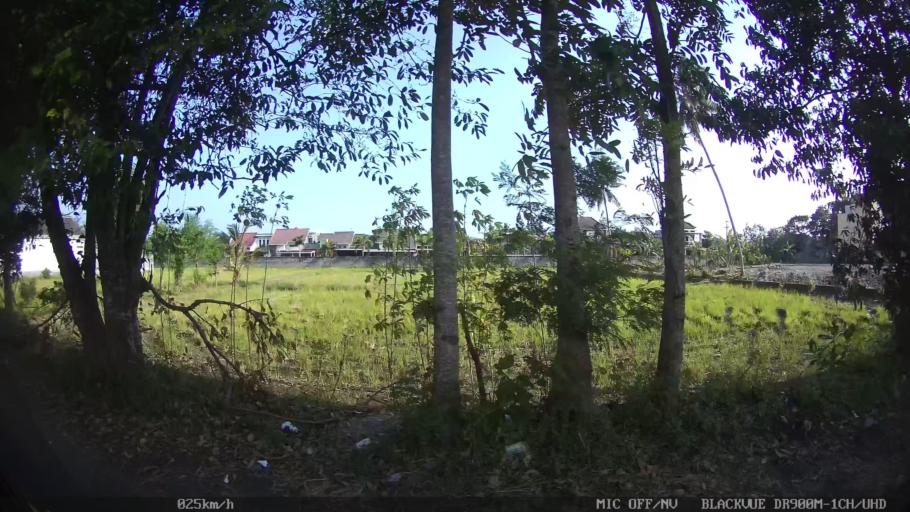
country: ID
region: Daerah Istimewa Yogyakarta
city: Gamping Lor
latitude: -7.7877
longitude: 110.3316
